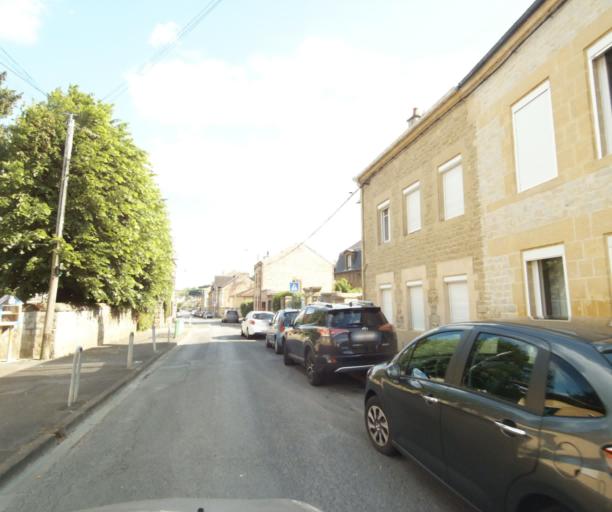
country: FR
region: Champagne-Ardenne
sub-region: Departement des Ardennes
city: Montcy-Notre-Dame
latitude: 49.7764
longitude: 4.7347
